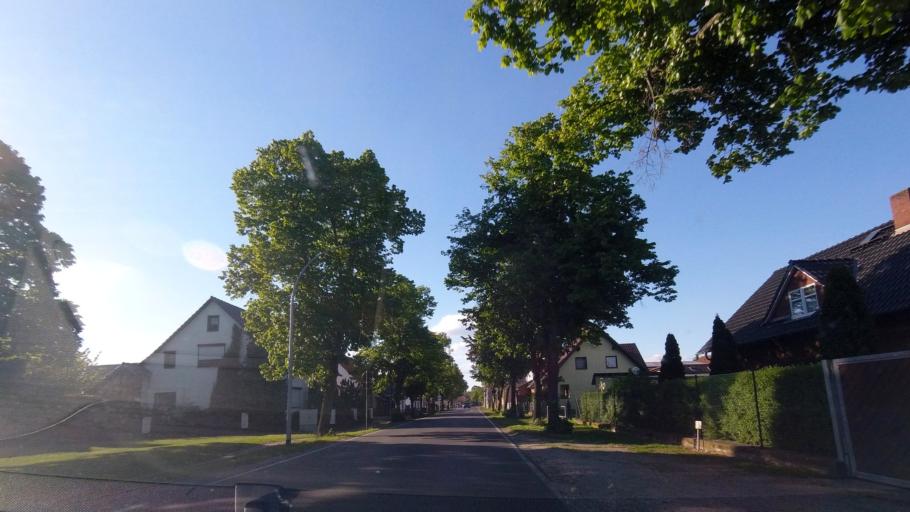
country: DE
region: Brandenburg
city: Luebben
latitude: 51.9309
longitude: 13.8932
